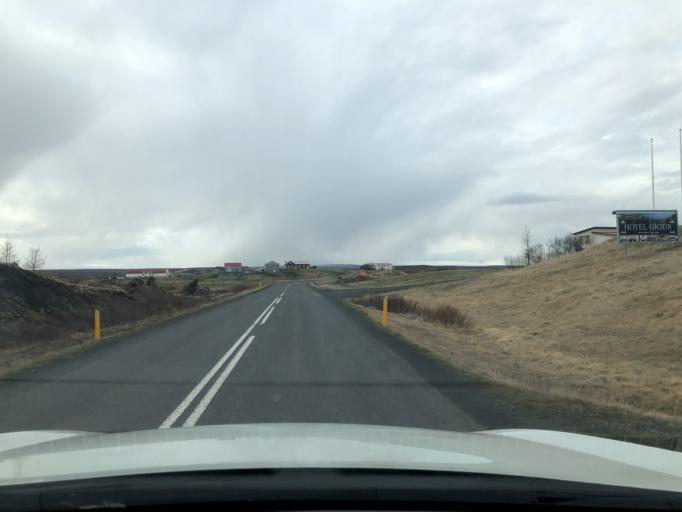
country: IS
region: Northeast
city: Laugar
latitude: 65.5677
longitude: -17.0380
